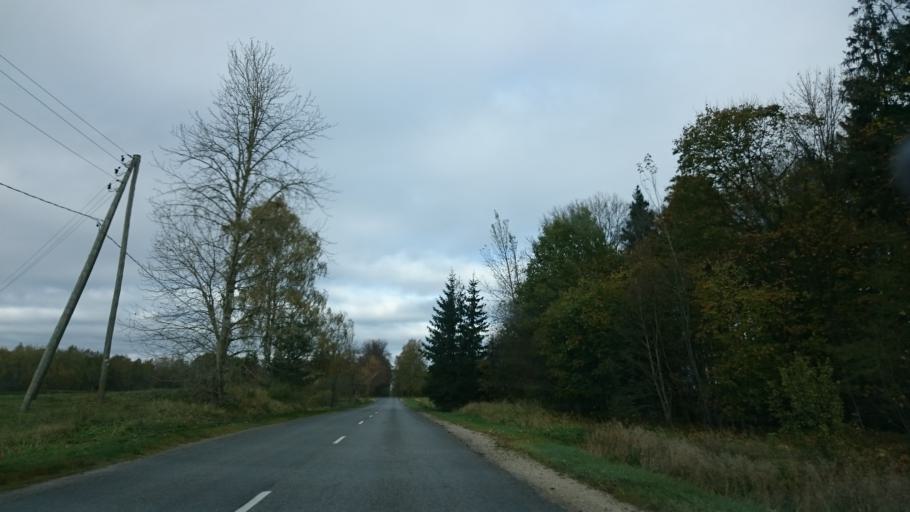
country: LV
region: Cesu Rajons
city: Cesis
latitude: 57.2855
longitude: 25.2654
